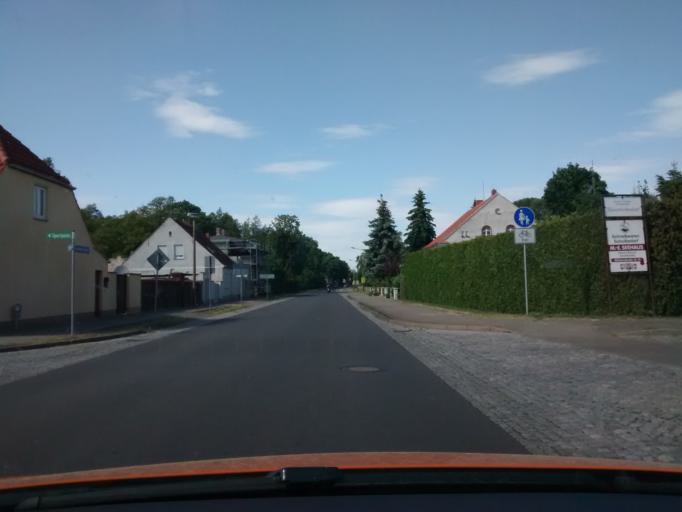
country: DE
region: Brandenburg
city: Juterbog
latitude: 52.0243
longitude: 13.1048
